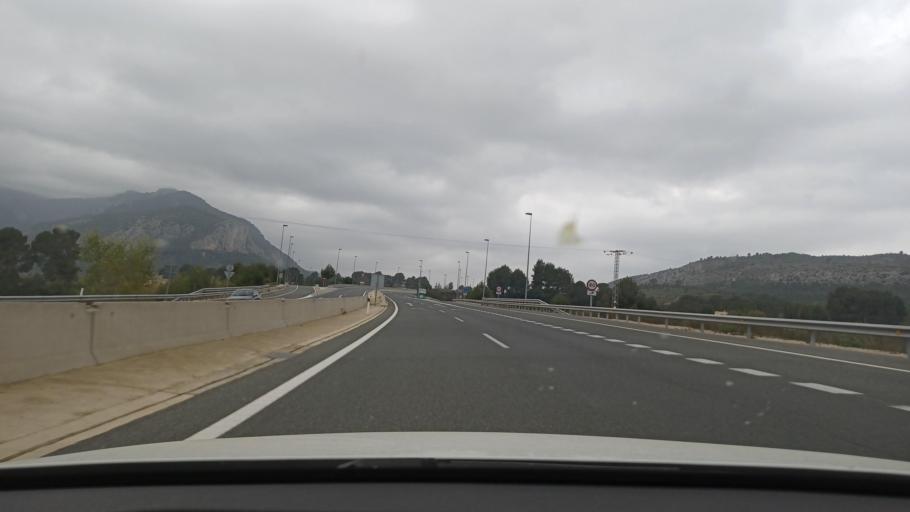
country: ES
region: Valencia
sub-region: Provincia de Alicante
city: Muro del Alcoy
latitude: 38.7946
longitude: -0.4440
